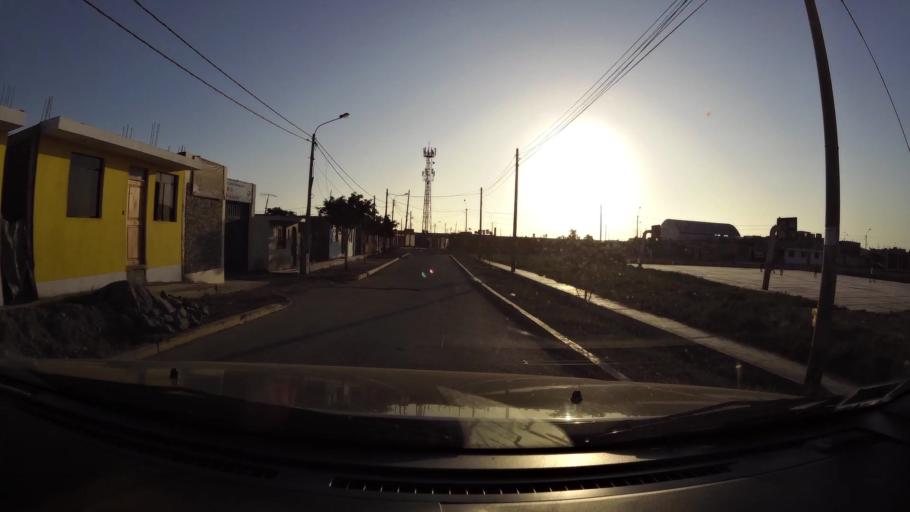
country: PE
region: Ica
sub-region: Provincia de Pisco
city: Villa Tupac Amaru
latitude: -13.7088
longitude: -76.1498
